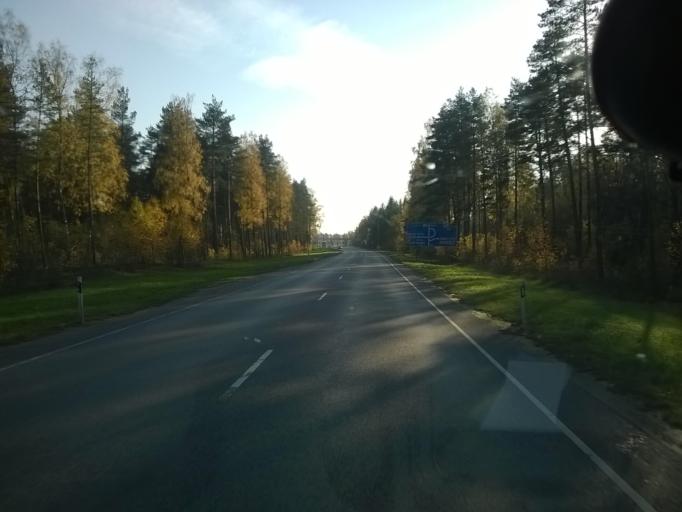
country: EE
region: Harju
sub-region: Saku vald
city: Saku
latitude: 59.3199
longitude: 24.6874
